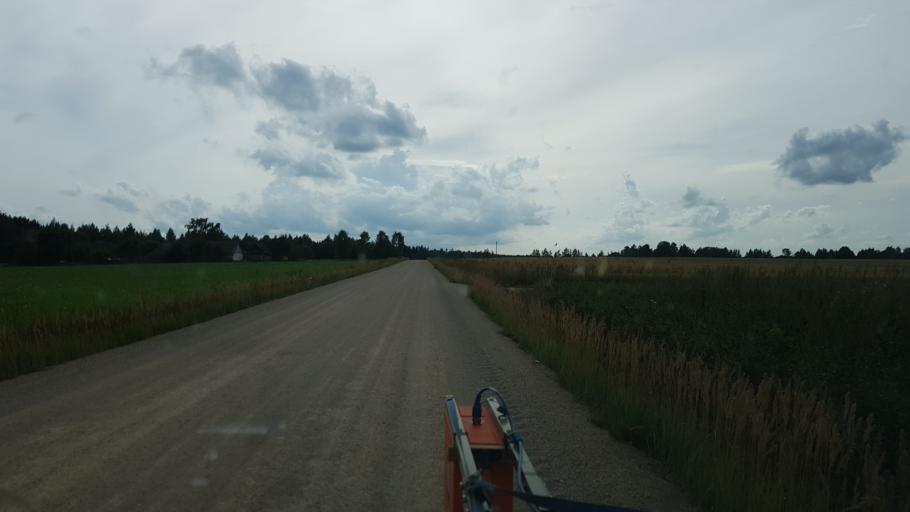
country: RU
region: Pskov
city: Pechory
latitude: 57.7940
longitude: 27.4858
